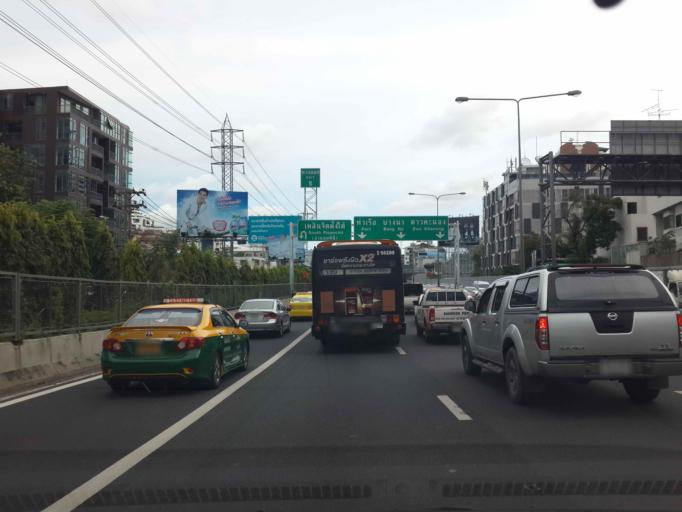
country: TH
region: Bangkok
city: Ratchathewi
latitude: 13.7403
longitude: 100.5508
